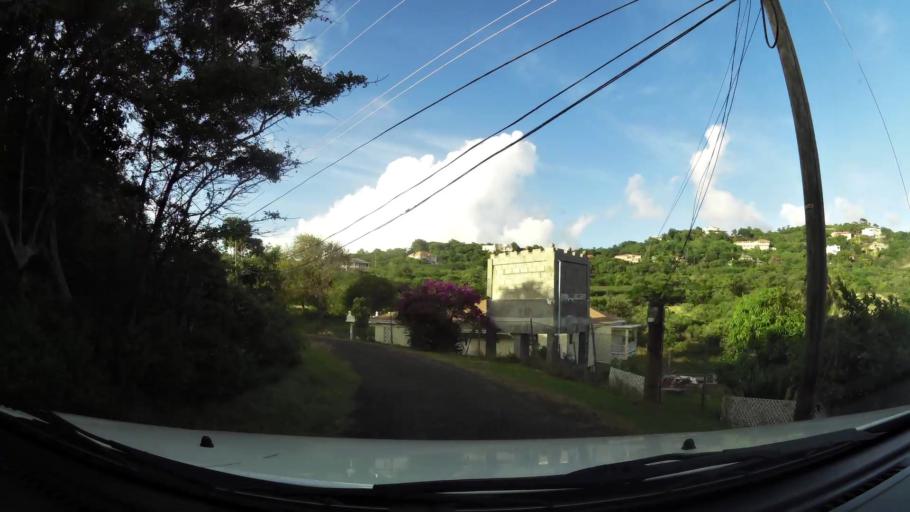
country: LC
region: Gros-Islet
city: Gros Islet
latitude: 14.0971
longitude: -60.9306
